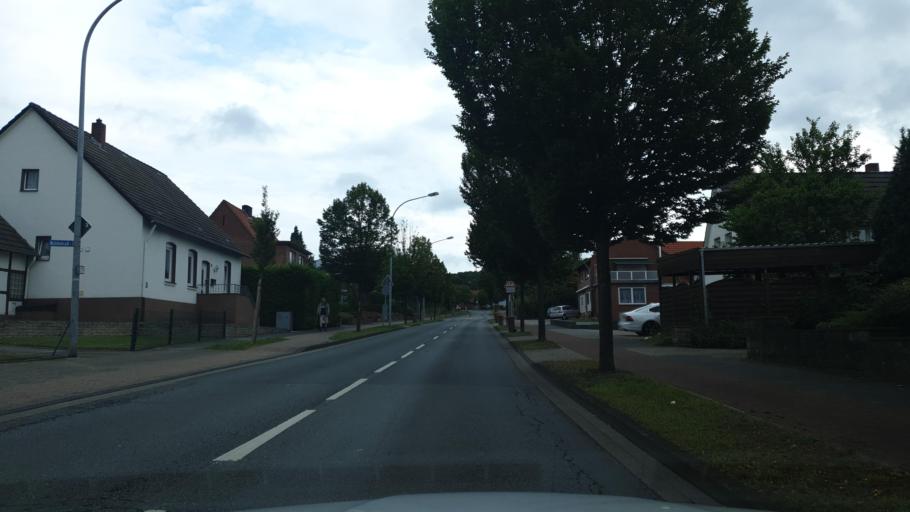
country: DE
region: North Rhine-Westphalia
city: Lengerich
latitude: 52.1866
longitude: 7.8642
